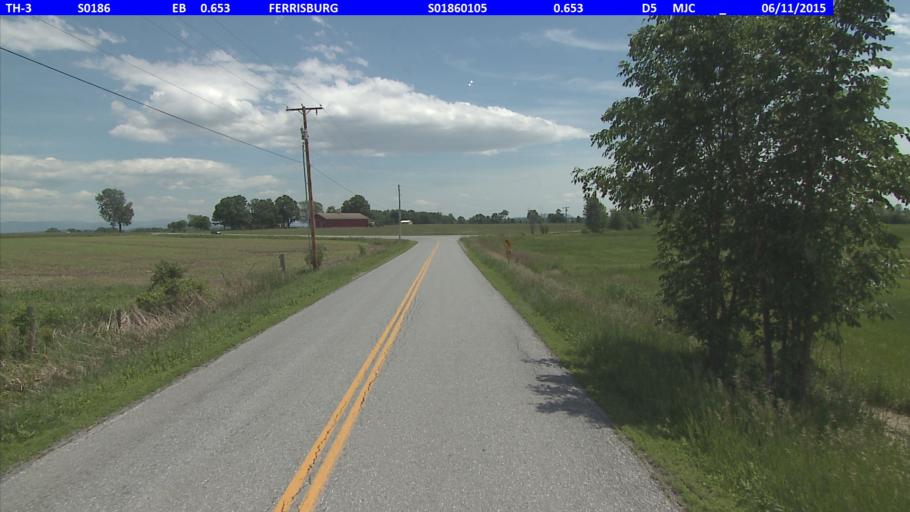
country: US
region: Vermont
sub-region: Addison County
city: Vergennes
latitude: 44.1945
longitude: -73.3511
